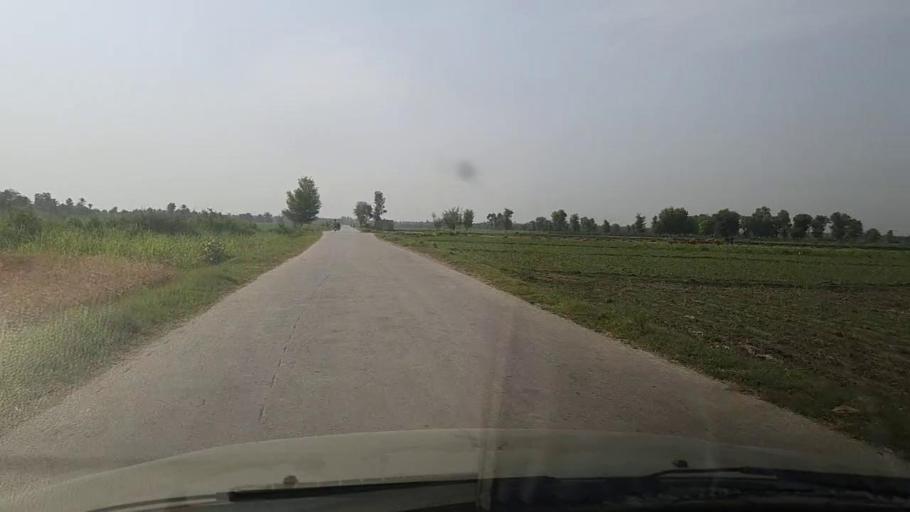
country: PK
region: Sindh
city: Gambat
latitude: 27.4658
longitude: 68.4786
